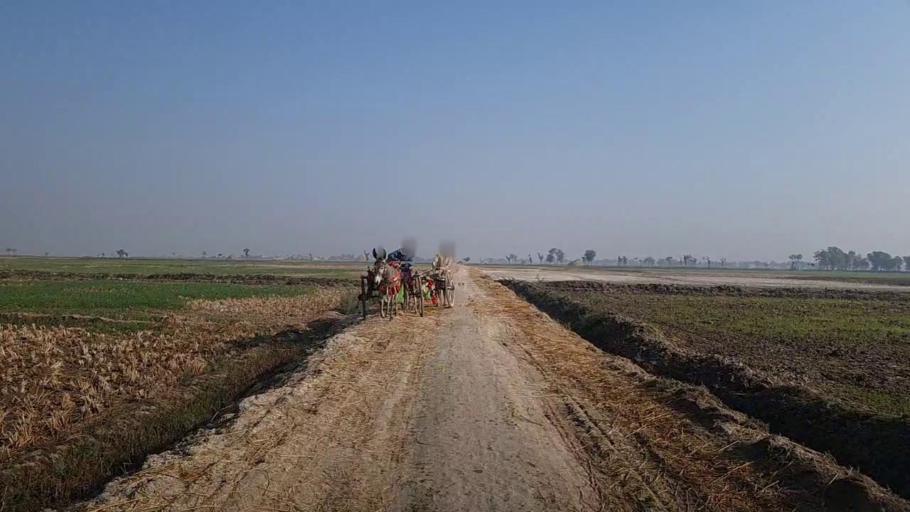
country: PK
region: Sindh
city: Sita Road
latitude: 27.1098
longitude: 67.8916
